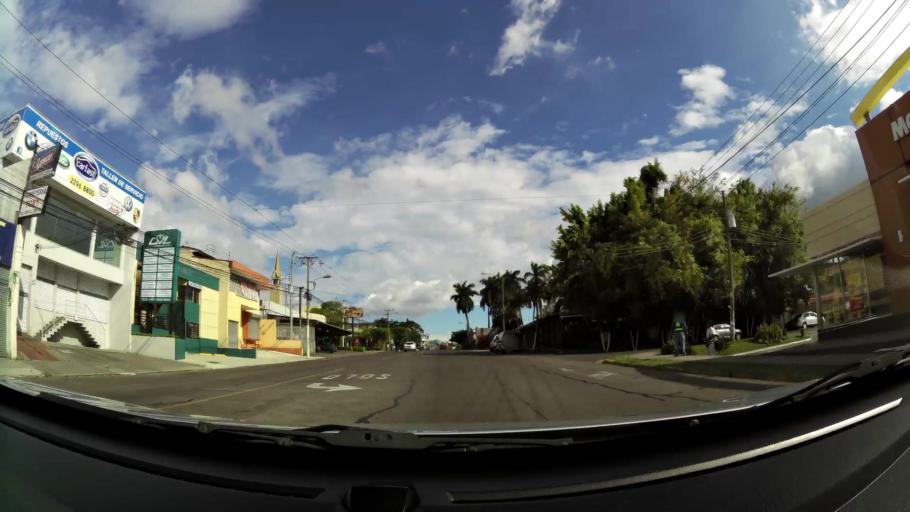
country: CR
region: San Jose
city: San Rafael
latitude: 9.9431
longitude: -84.1265
